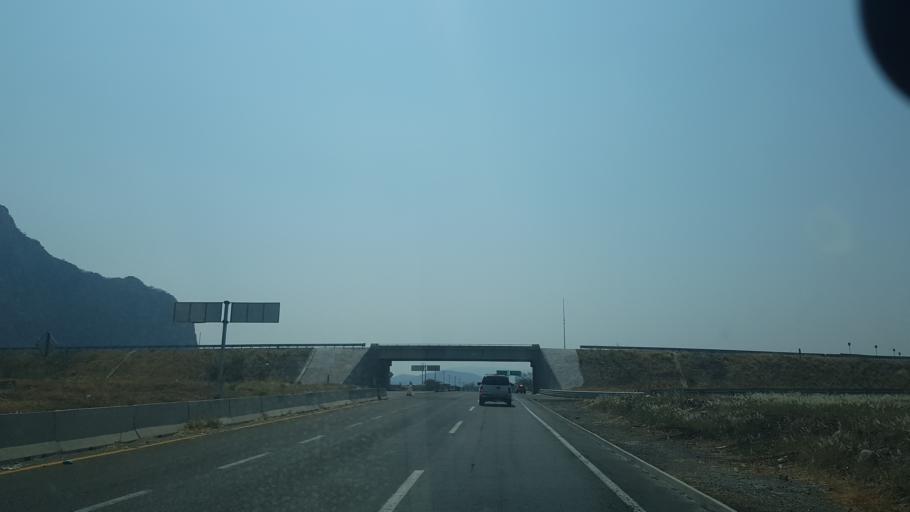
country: MX
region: Morelos
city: Jantetelco
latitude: 18.7032
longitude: -98.7696
